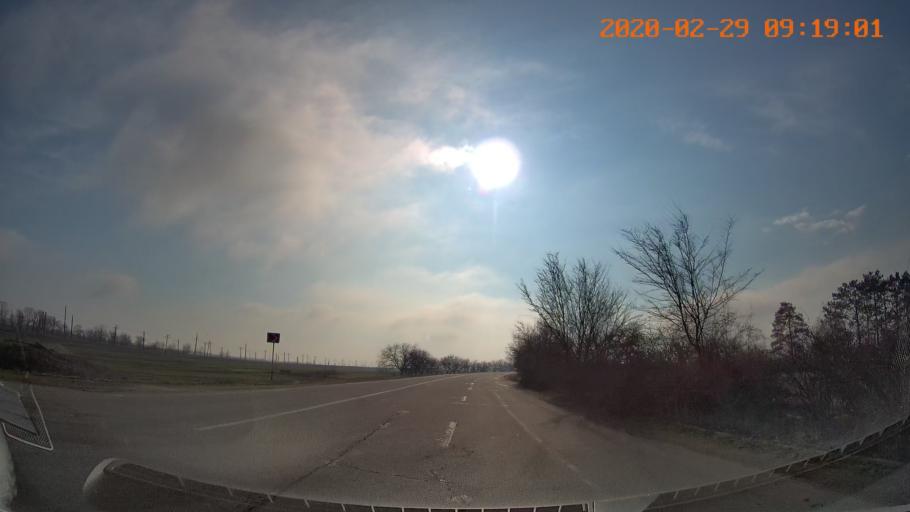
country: MD
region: Telenesti
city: Pervomaisc
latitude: 46.7681
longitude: 29.9338
